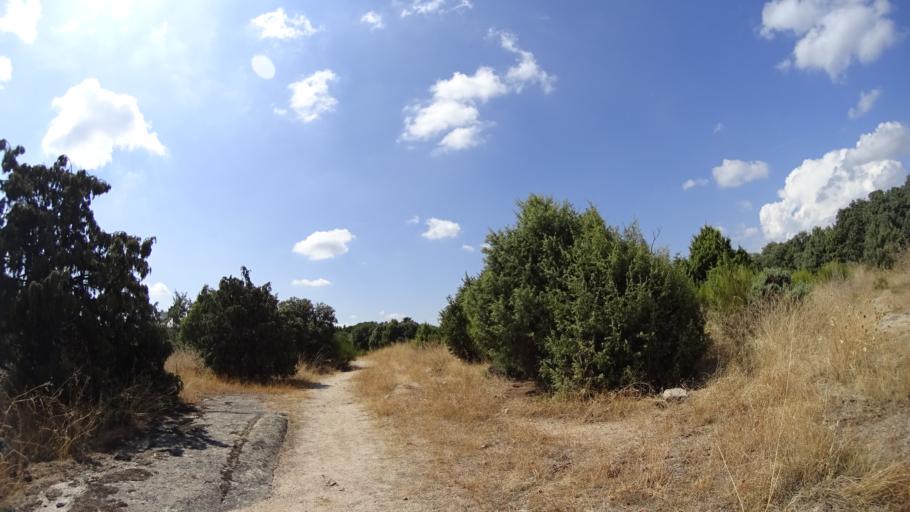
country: ES
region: Madrid
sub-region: Provincia de Madrid
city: Galapagar
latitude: 40.5919
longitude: -3.9901
